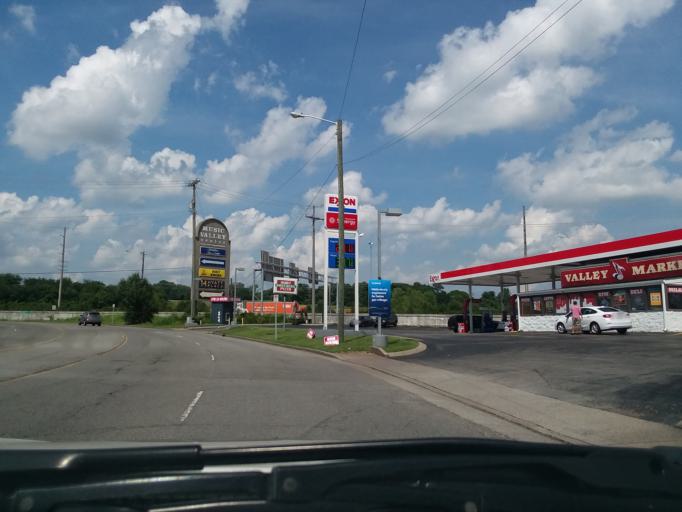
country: US
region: Tennessee
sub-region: Davidson County
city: Lakewood
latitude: 36.2190
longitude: -86.6943
